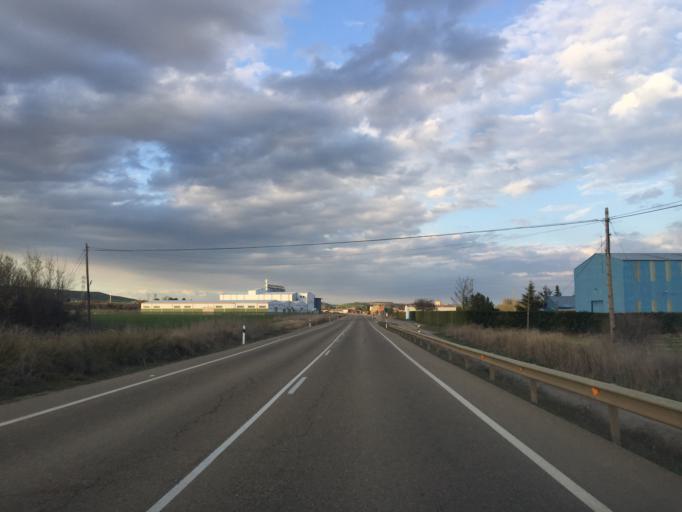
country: ES
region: Castille and Leon
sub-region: Provincia de Palencia
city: Soto de Cerrato
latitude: 41.9748
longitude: -4.4369
